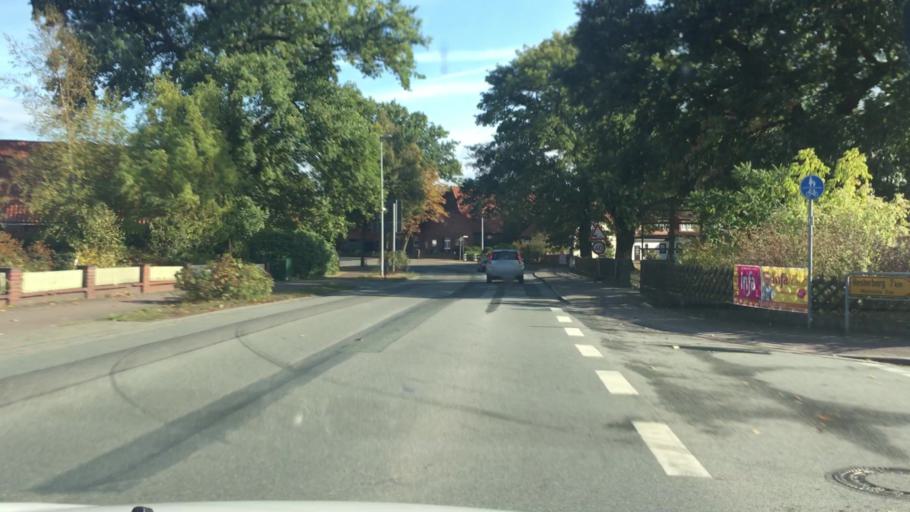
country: DE
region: Lower Saxony
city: Borstel
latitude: 52.6689
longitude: 8.9727
